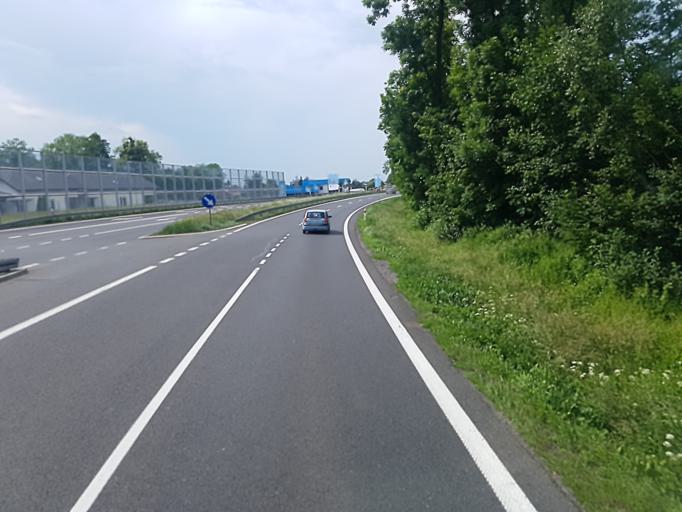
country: PL
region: Silesian Voivodeship
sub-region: Powiat cieszynski
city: Ochaby
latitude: 49.8357
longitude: 18.7759
